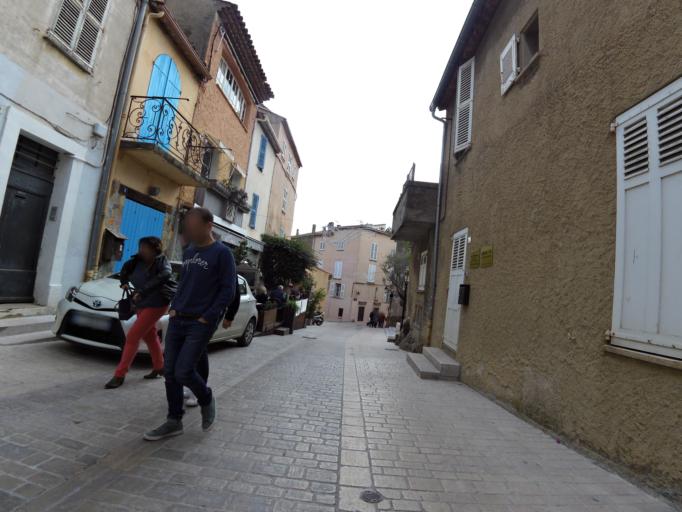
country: FR
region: Provence-Alpes-Cote d'Azur
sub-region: Departement du Var
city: Saint-Tropez
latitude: 43.2719
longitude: 6.6412
